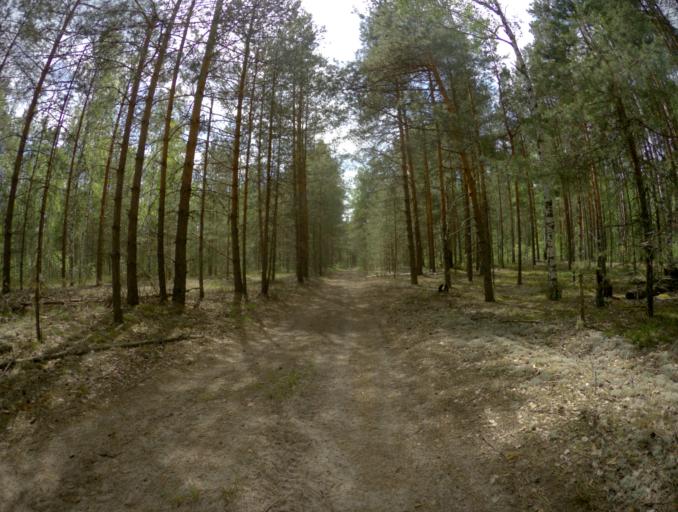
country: RU
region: Vladimir
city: Ivanishchi
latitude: 55.6933
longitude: 40.4255
